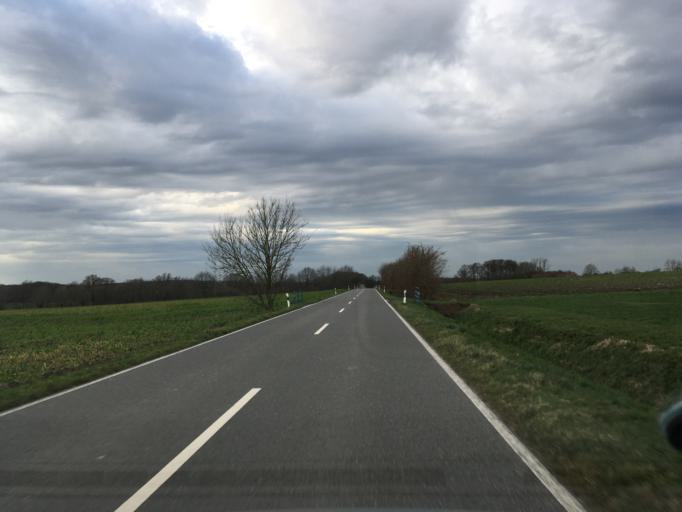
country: DE
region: North Rhine-Westphalia
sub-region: Regierungsbezirk Munster
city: Legden
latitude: 52.0551
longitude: 7.1717
